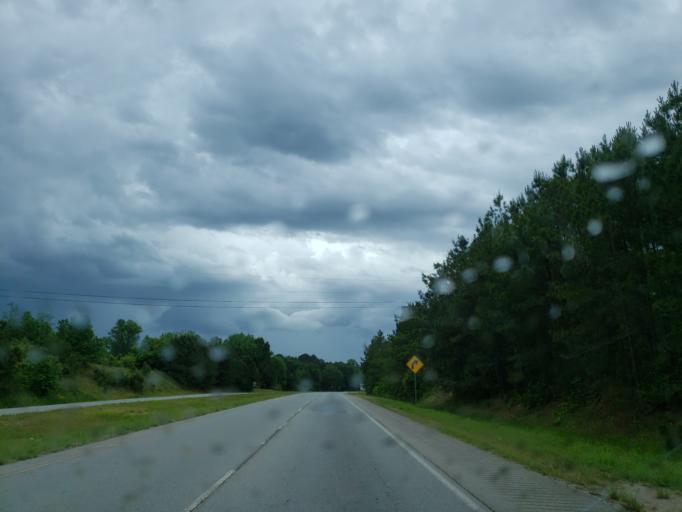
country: US
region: Georgia
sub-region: Haralson County
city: Buchanan
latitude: 33.9081
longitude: -85.2389
